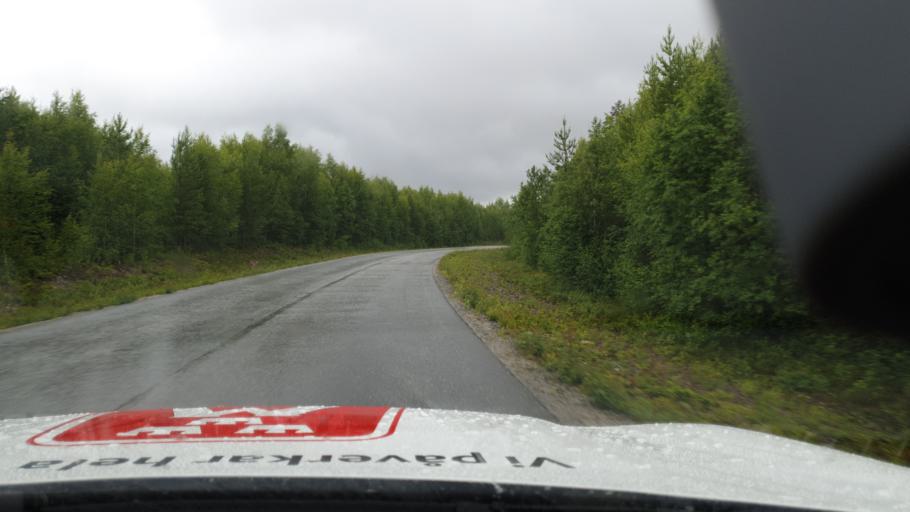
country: SE
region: Vaesterbotten
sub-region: Vindelns Kommun
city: Vindeln
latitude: 64.3211
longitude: 19.6211
